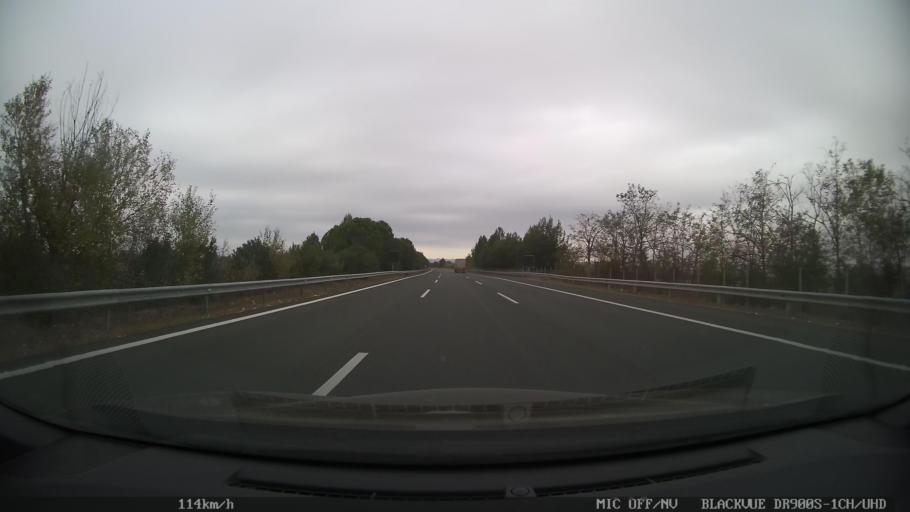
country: GR
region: Central Macedonia
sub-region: Nomos Imathias
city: Kleidi
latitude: 40.5311
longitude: 22.5772
